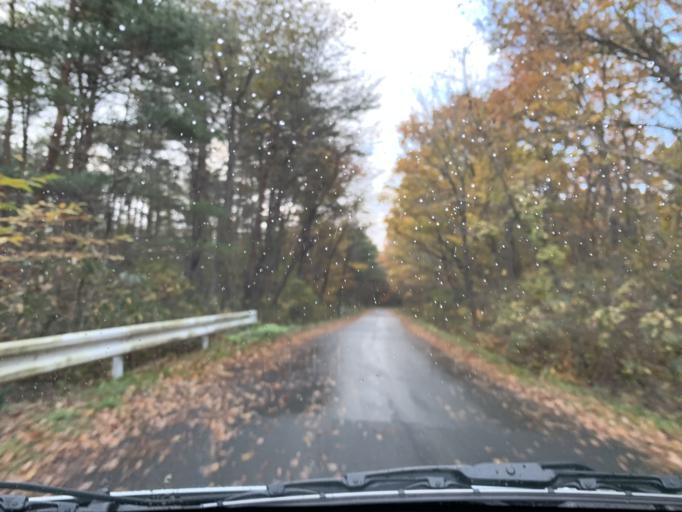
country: JP
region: Iwate
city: Mizusawa
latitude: 39.0761
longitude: 141.0270
